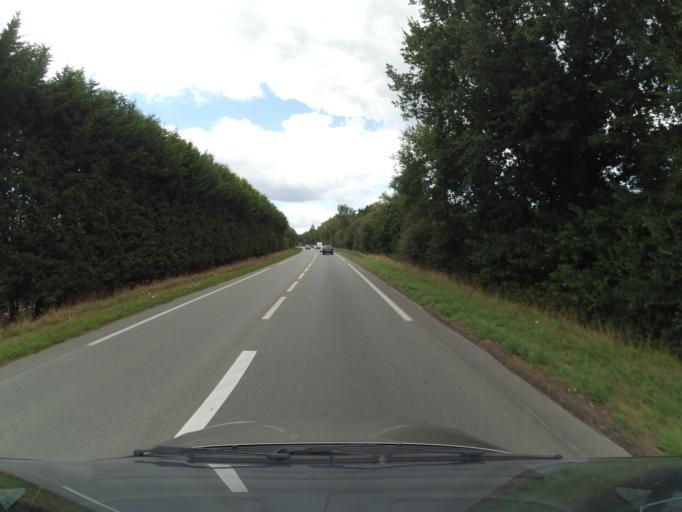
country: FR
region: Brittany
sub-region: Departement du Morbihan
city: Merlevenez
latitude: 47.7419
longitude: -3.2258
